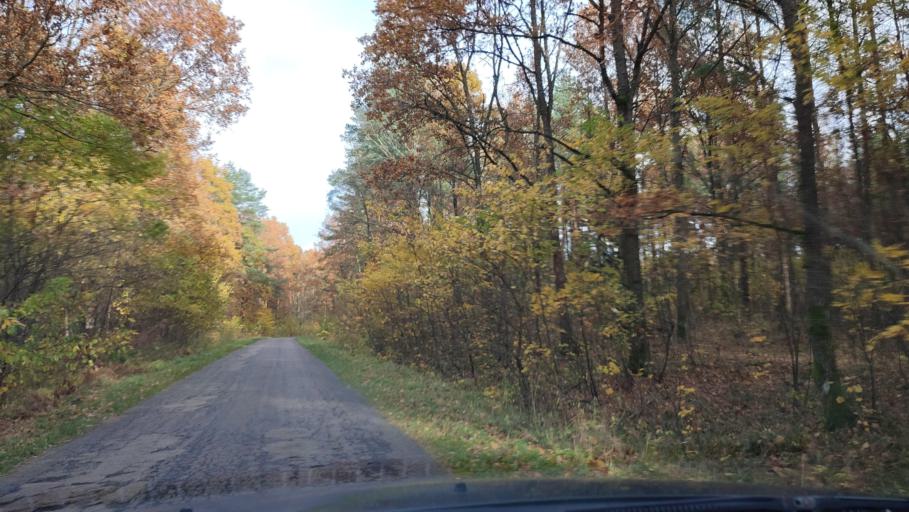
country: PL
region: Warmian-Masurian Voivodeship
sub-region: Powiat szczycienski
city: Szczytno
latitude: 53.5273
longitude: 20.9181
